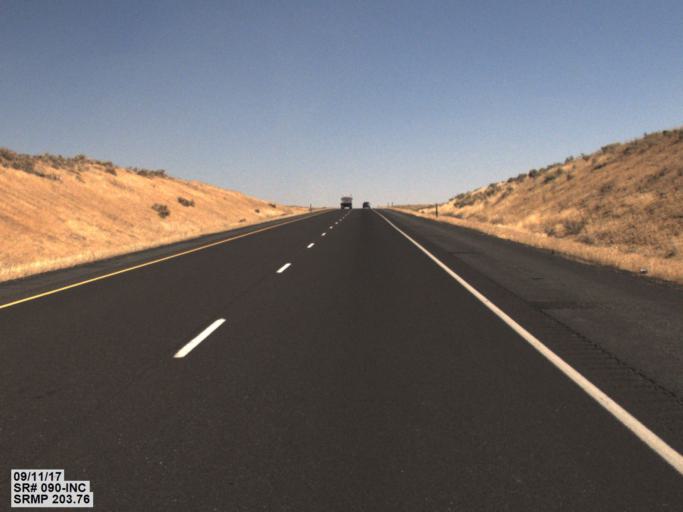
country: US
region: Washington
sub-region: Grant County
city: Warden
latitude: 47.0861
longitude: -118.7301
